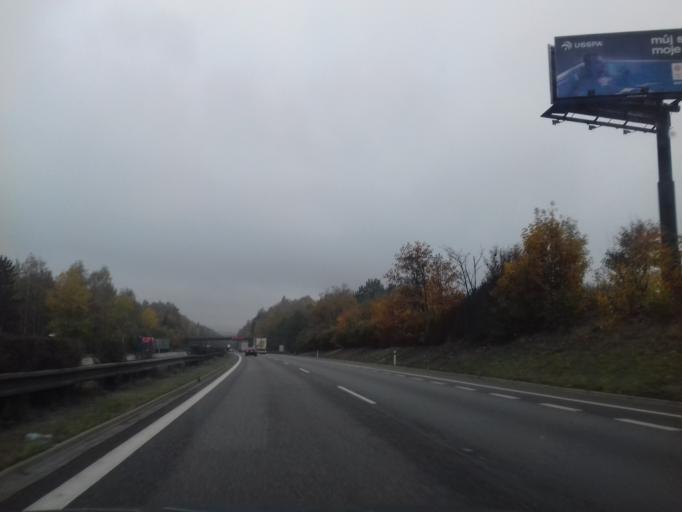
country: CZ
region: Vysocina
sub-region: Okres Pelhrimov
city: Zeliv
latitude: 49.5678
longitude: 15.2841
